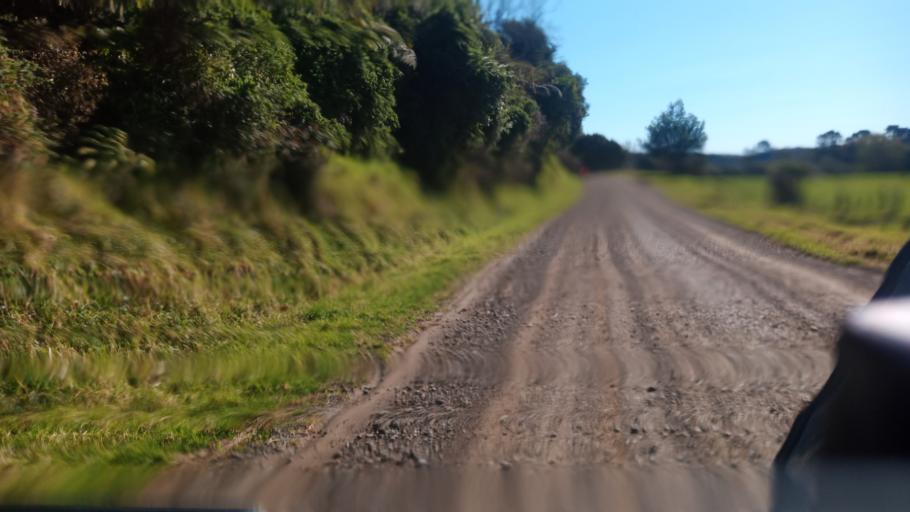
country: NZ
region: Bay of Plenty
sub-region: Opotiki District
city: Opotiki
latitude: -38.0186
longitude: 177.4319
